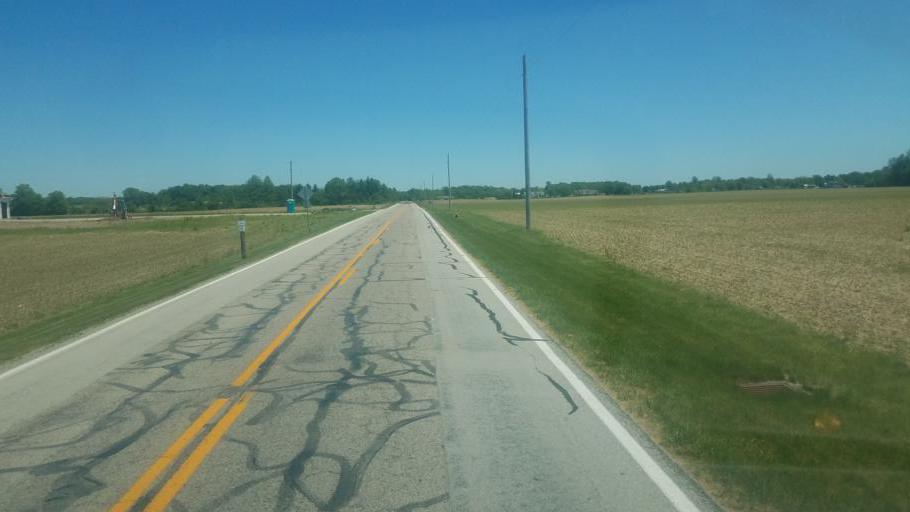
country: US
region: Ohio
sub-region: Miami County
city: Covington
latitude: 40.2316
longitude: -84.3652
